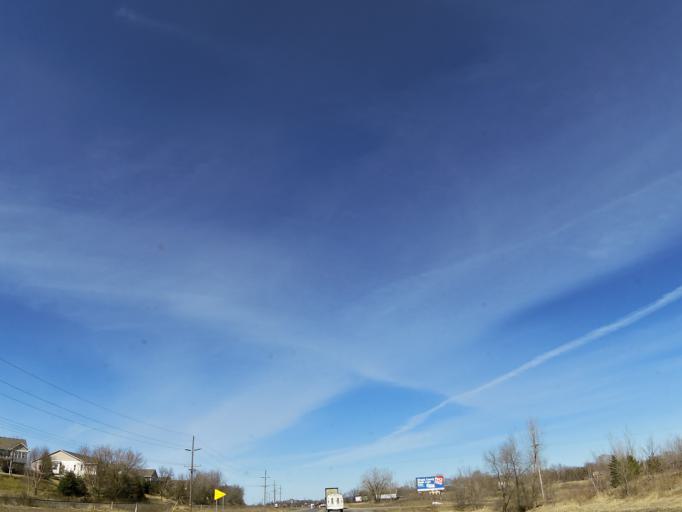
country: US
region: Minnesota
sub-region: Wright County
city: Buffalo
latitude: 45.1876
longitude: -93.8837
